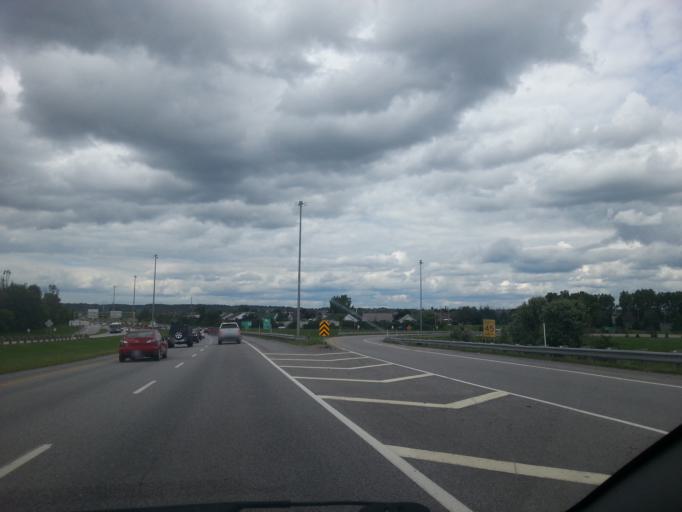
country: CA
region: Quebec
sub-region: Outaouais
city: Gatineau
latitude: 45.4723
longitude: -75.7137
